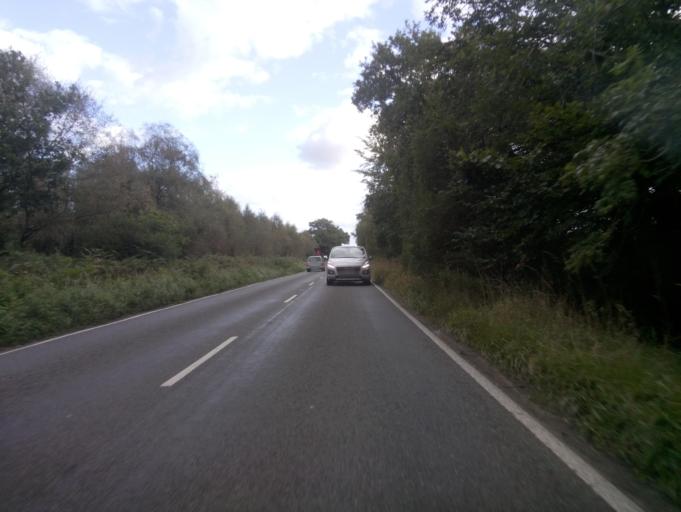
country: GB
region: England
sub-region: Devon
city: Honiton
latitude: 50.7616
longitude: -3.2128
